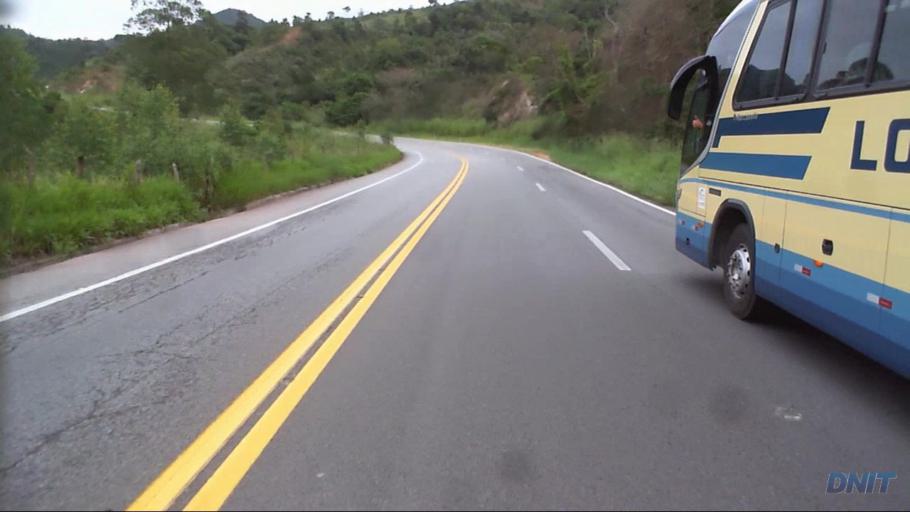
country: BR
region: Minas Gerais
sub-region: Nova Era
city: Nova Era
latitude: -19.6274
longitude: -42.8719
